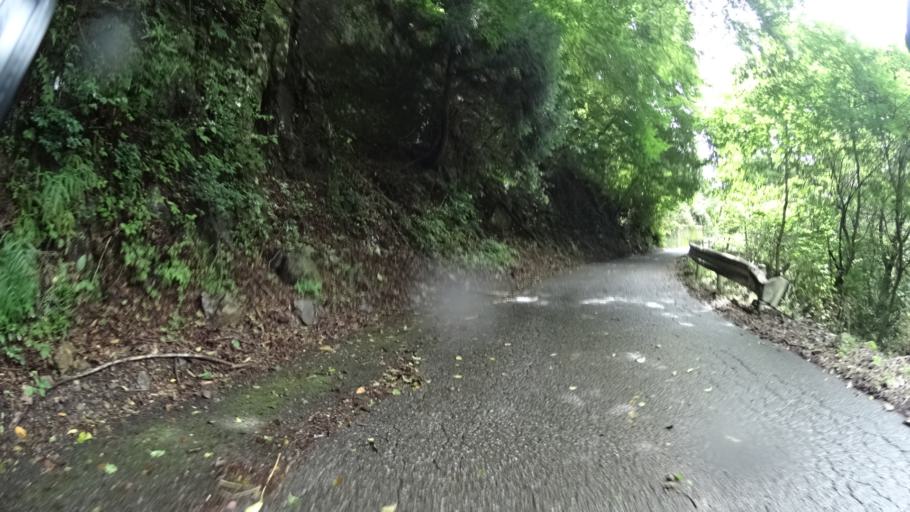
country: JP
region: Saitama
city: Chichibu
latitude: 35.8872
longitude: 139.1332
